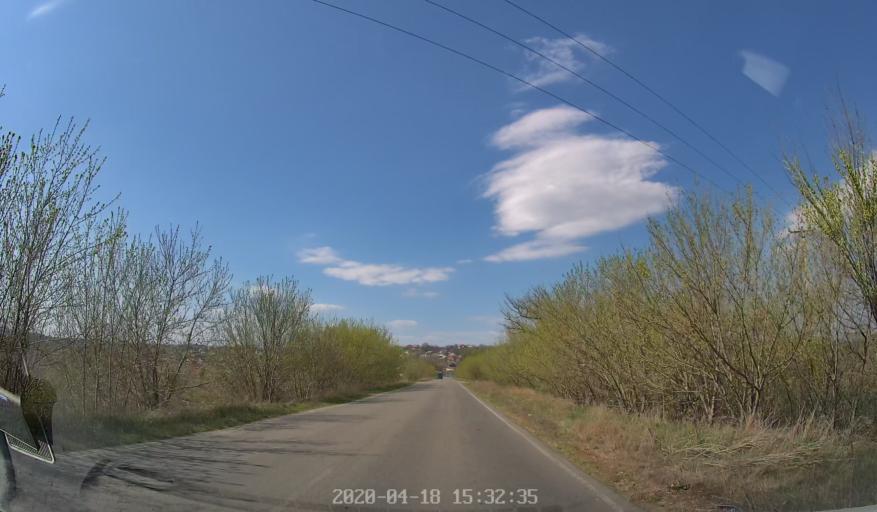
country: MD
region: Chisinau
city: Vadul lui Voda
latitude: 47.1114
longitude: 29.0602
